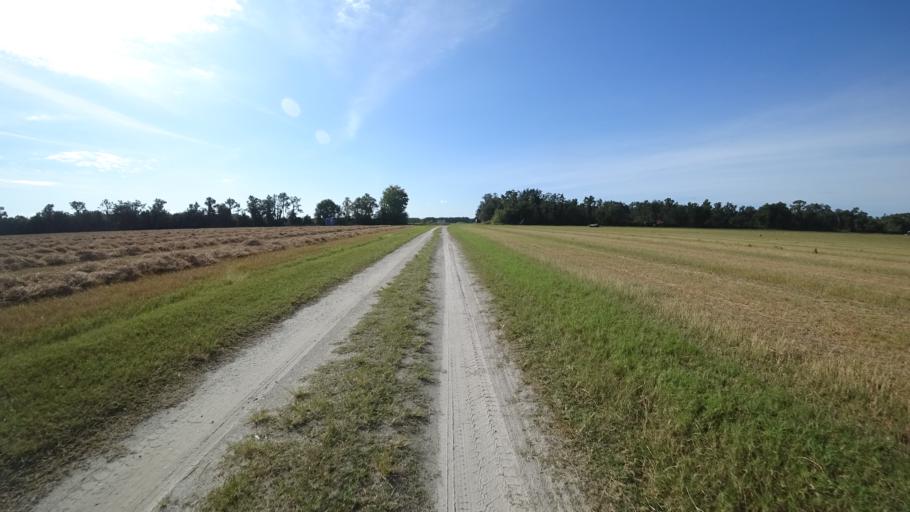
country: US
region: Florida
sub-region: Hillsborough County
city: Wimauma
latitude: 27.6432
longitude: -82.2989
